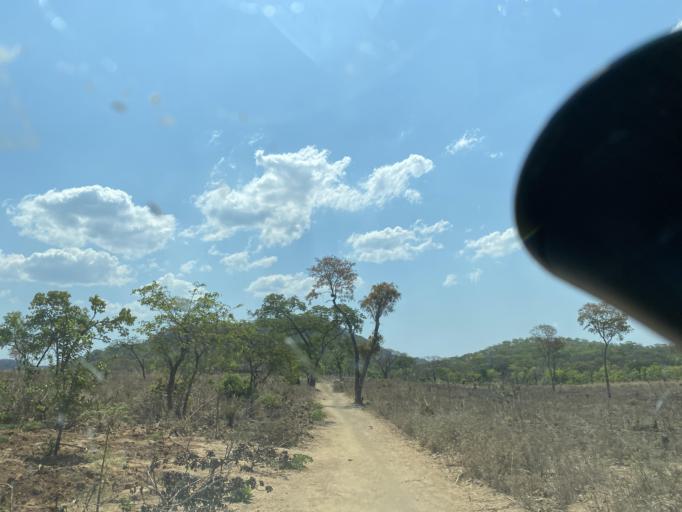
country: ZM
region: Lusaka
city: Chongwe
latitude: -15.0832
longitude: 29.4728
